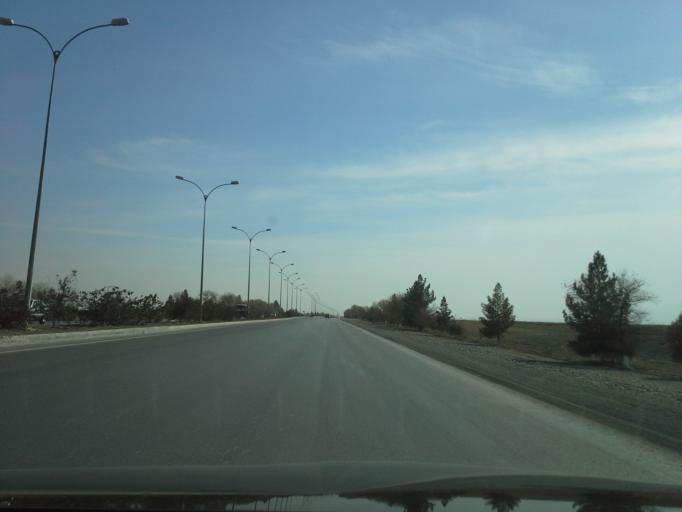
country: TM
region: Ahal
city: Abadan
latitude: 38.1261
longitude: 58.0319
